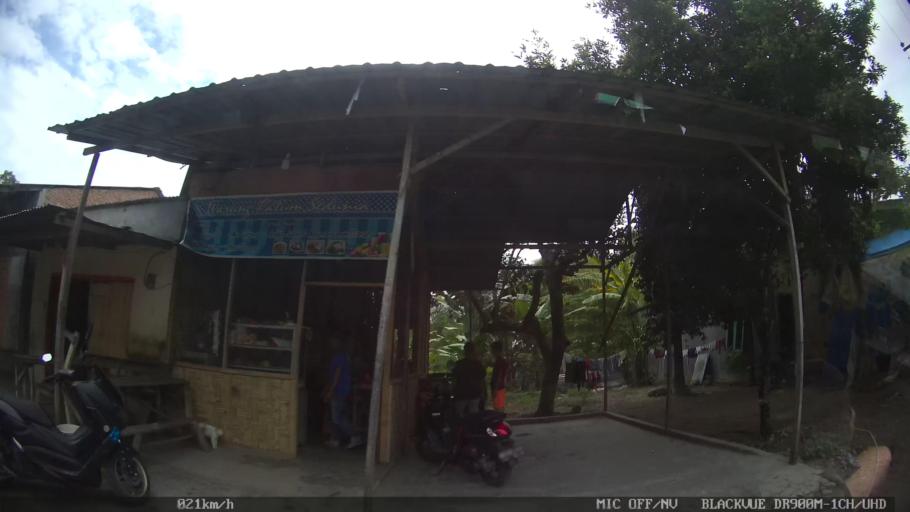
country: ID
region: North Sumatra
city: Sunggal
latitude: 3.6477
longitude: 98.5924
